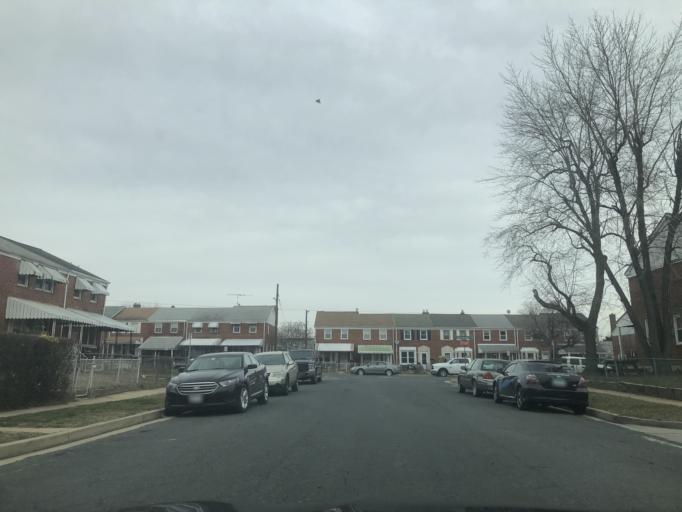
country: US
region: Maryland
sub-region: Baltimore County
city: Dundalk
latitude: 39.2622
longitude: -76.4904
